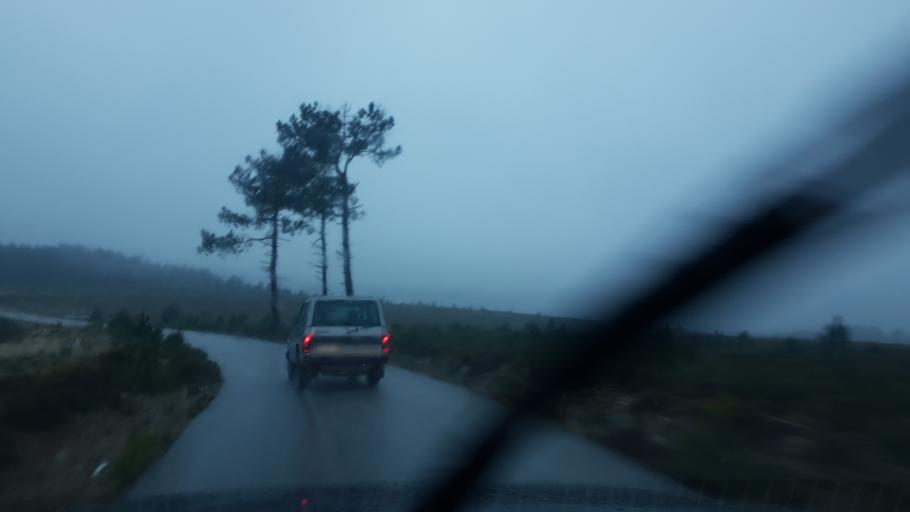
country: PT
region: Viseu
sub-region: Sao Pedro do Sul
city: Sao Pedro do Sul
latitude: 40.8313
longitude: -8.1324
